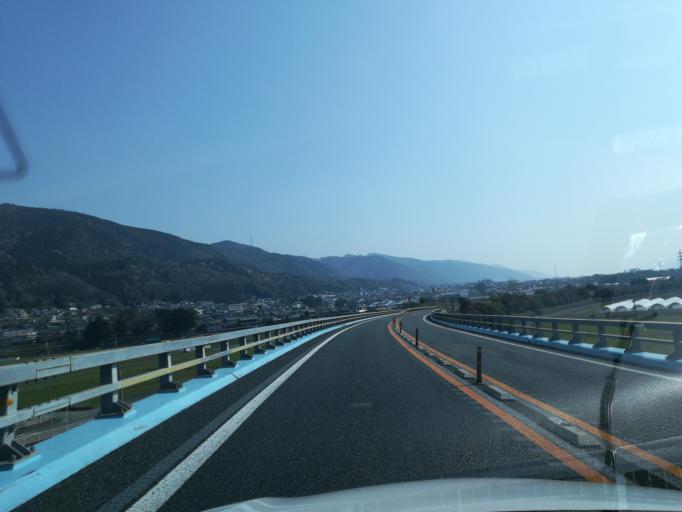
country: JP
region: Tokushima
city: Ikedacho
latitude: 34.0359
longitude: 133.8666
